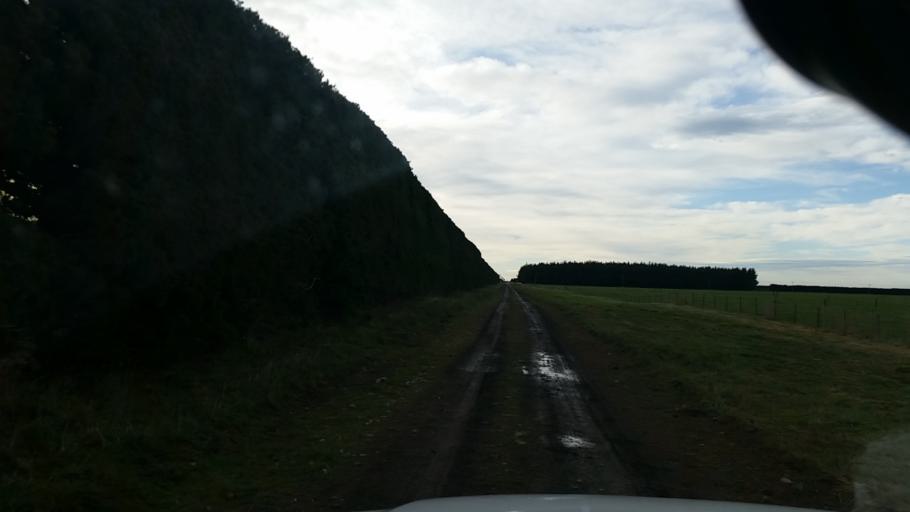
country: NZ
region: Canterbury
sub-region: Ashburton District
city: Tinwald
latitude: -44.0601
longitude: 171.4356
